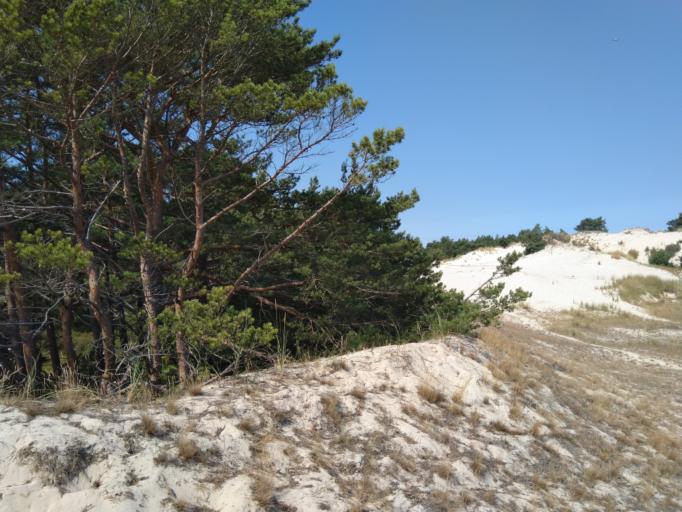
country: PL
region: Pomeranian Voivodeship
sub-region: Powiat pucki
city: Hel
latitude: 54.6572
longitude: 18.7720
